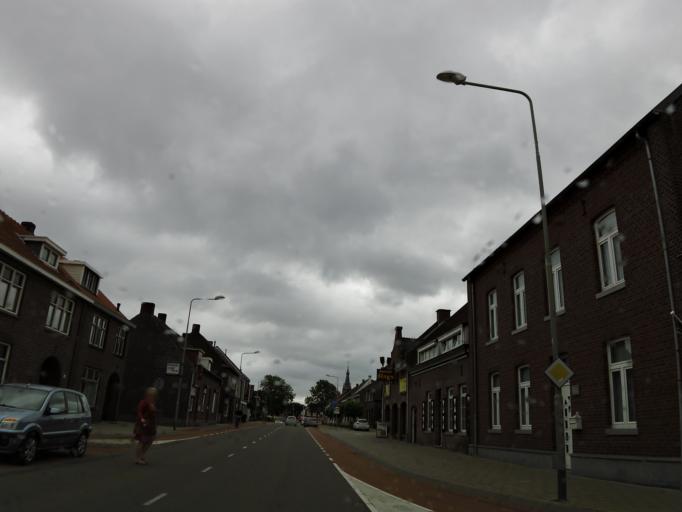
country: NL
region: Limburg
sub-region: Gemeente Maasgouw
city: Maasbracht
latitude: 51.0980
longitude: 5.8817
